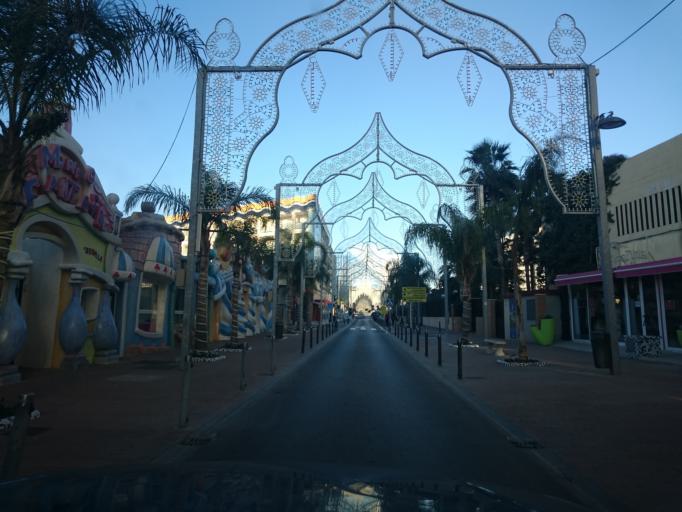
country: ES
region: Valencia
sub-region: Provincia de Castello
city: Orpesa/Oropesa del Mar
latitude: 40.1079
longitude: 0.1509
